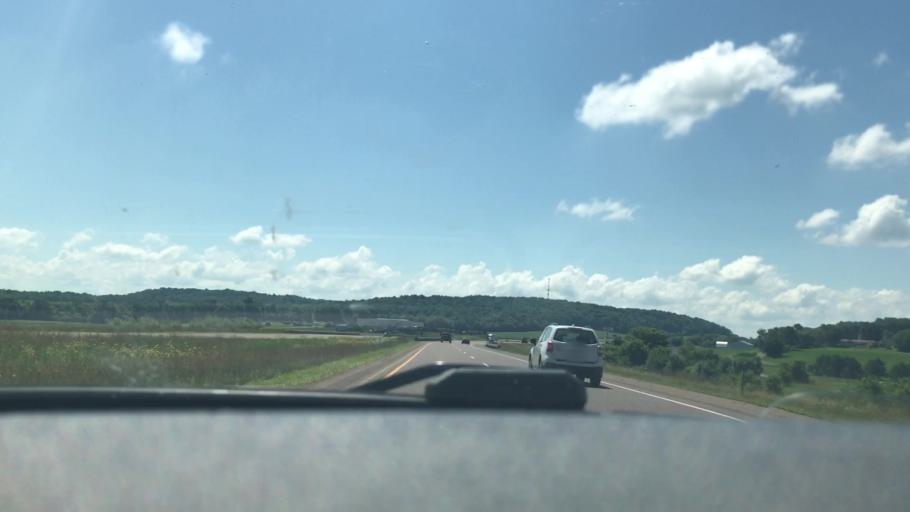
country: US
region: Wisconsin
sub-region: Chippewa County
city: Chippewa Falls
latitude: 44.9684
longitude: -91.4292
